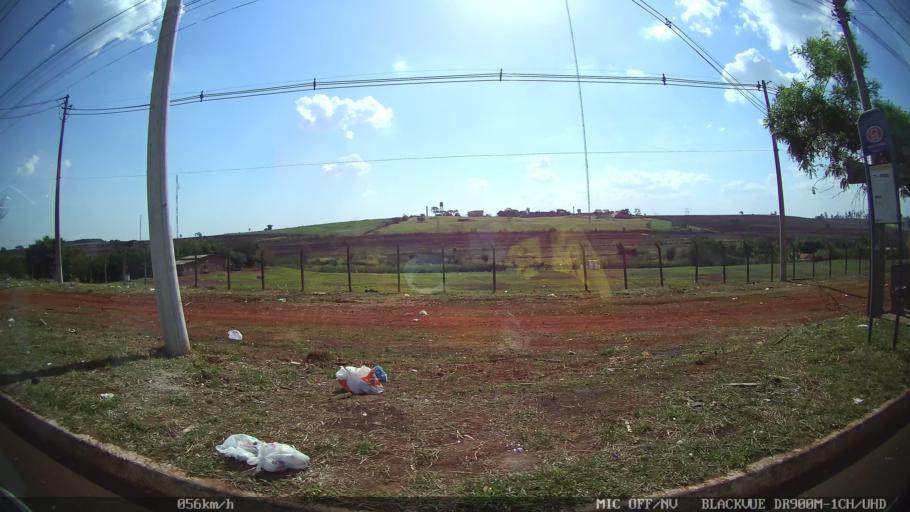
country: BR
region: Sao Paulo
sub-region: Ribeirao Preto
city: Ribeirao Preto
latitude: -21.1994
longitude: -47.8554
